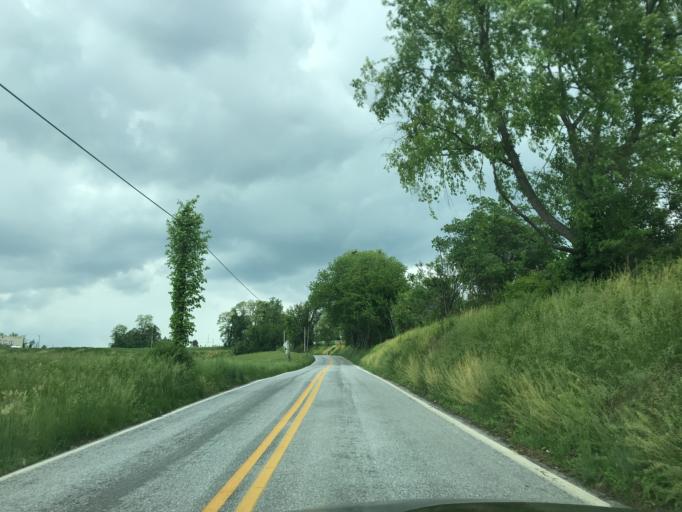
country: US
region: Pennsylvania
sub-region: York County
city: Susquehanna Trails
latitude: 39.7221
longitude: -76.3396
